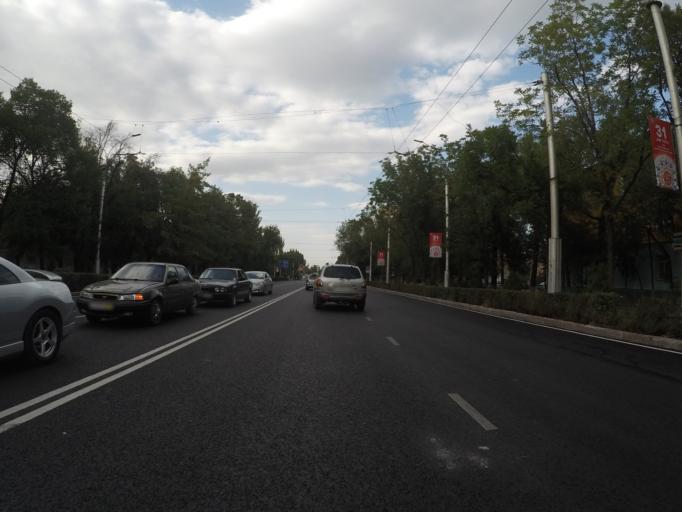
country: KG
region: Chuy
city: Bishkek
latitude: 42.8578
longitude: 74.5869
